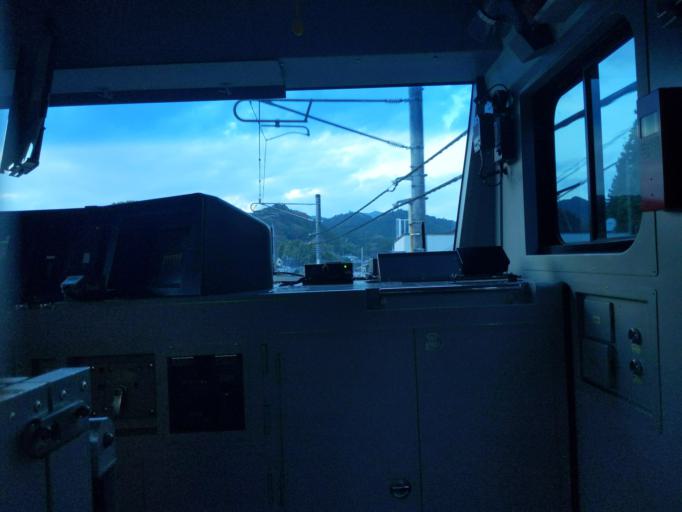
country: JP
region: Tokyo
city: Itsukaichi
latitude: 35.7339
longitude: 139.2318
